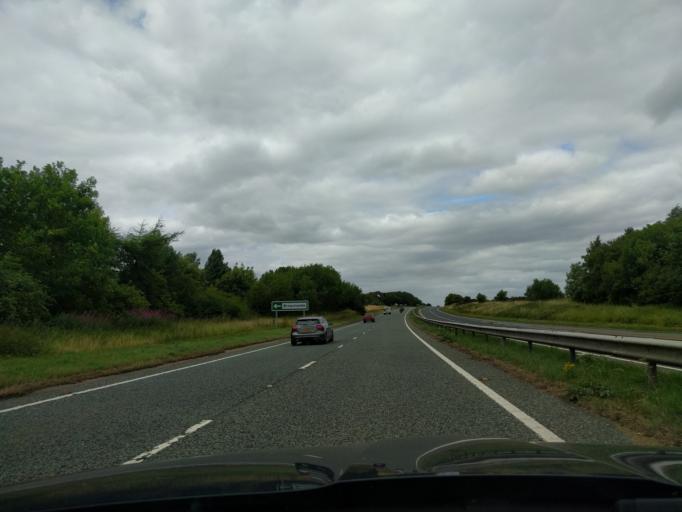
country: GB
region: England
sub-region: Northumberland
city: Ellingham
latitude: 55.5040
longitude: -1.7358
